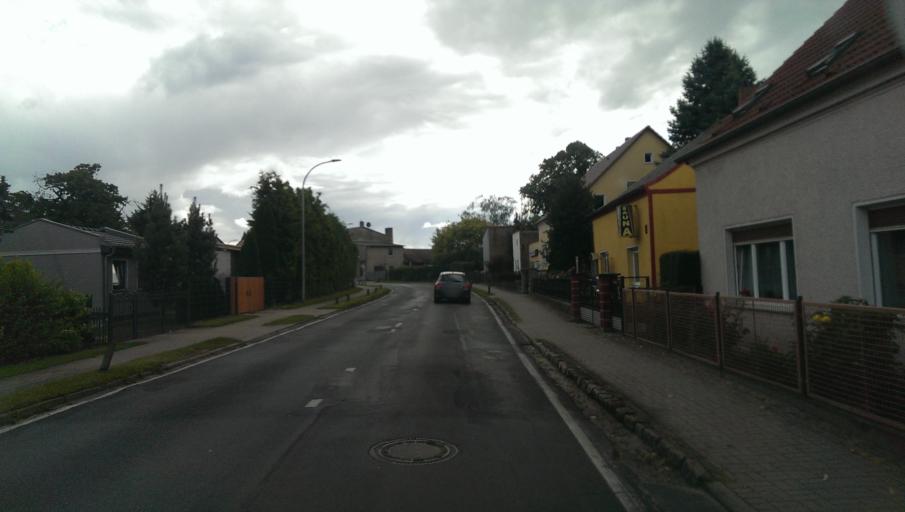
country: DE
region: Brandenburg
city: Velten
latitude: 52.6755
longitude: 13.1516
